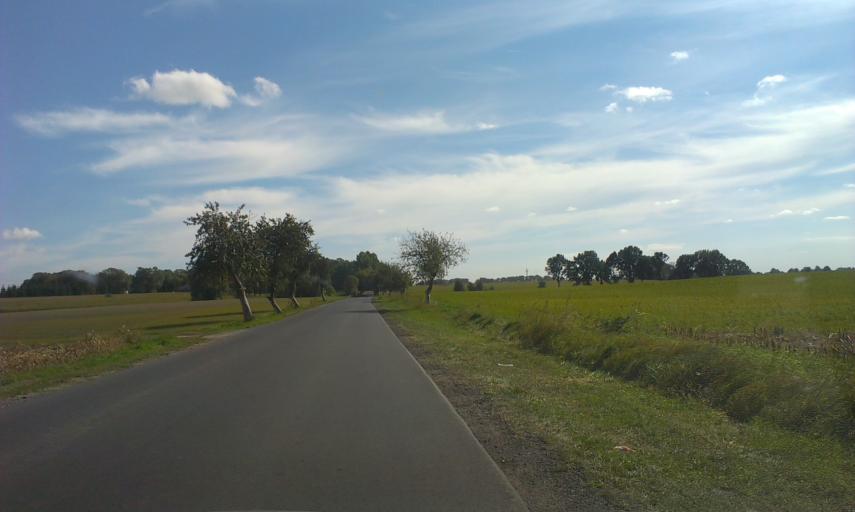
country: PL
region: Greater Poland Voivodeship
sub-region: Powiat pilski
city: Lobzenica
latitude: 53.2729
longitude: 17.2307
